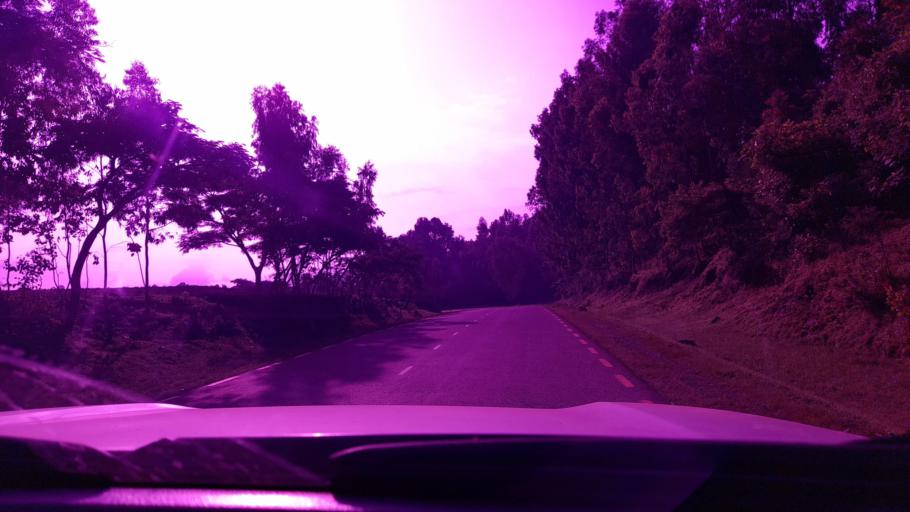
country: ET
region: Oromiya
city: Bedele
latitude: 8.1504
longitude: 36.4628
